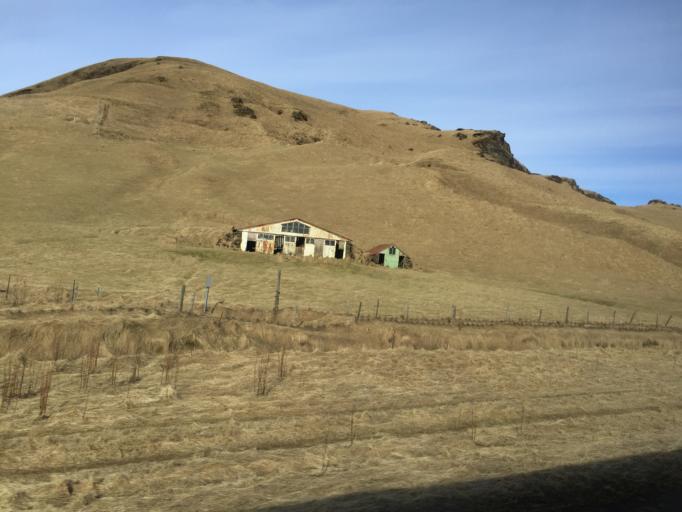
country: IS
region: South
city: Vestmannaeyjar
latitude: 63.4475
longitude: -19.1213
